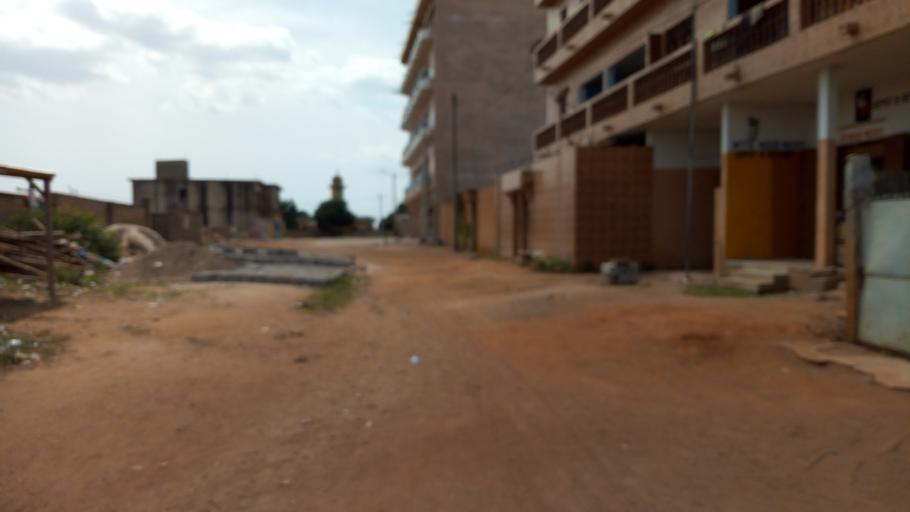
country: CI
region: Vallee du Bandama
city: Bouake
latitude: 7.7045
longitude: -5.0473
